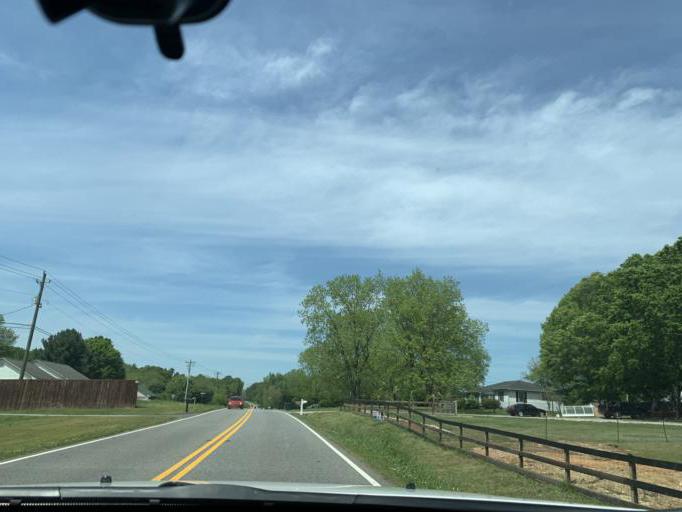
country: US
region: Georgia
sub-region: Forsyth County
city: Cumming
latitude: 34.2475
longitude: -84.1702
